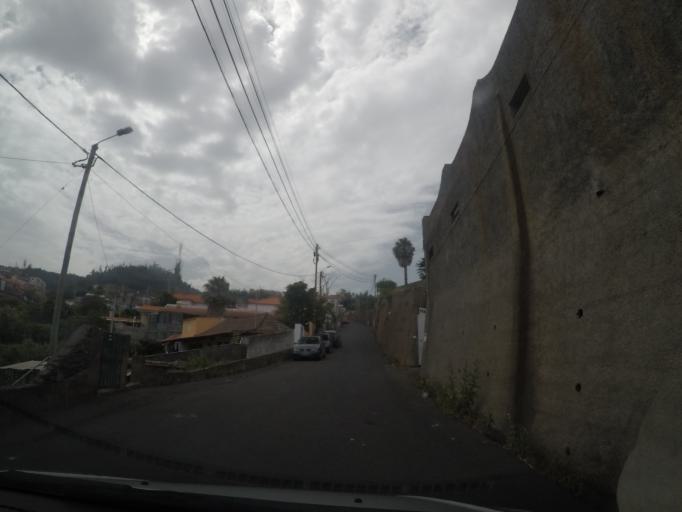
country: PT
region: Madeira
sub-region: Santa Cruz
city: Santa Cruz
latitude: 32.6886
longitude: -16.8107
